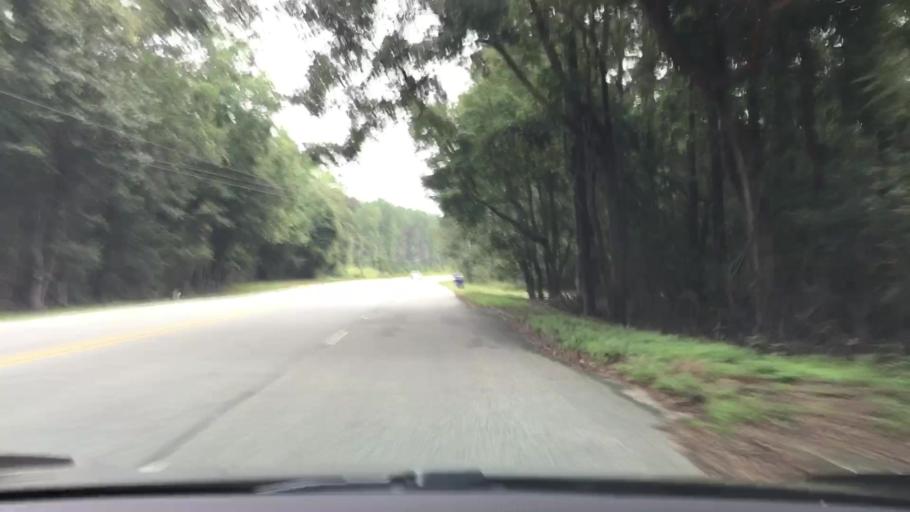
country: US
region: Alabama
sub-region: Coffee County
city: Elba
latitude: 31.4561
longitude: -86.0692
